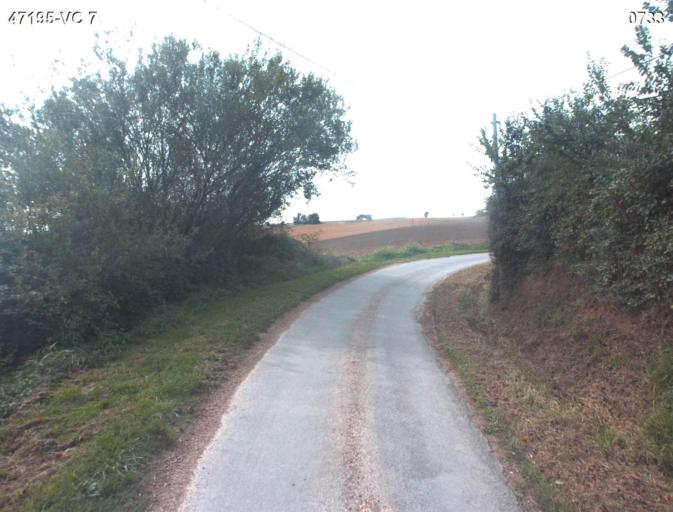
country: FR
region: Aquitaine
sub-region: Departement du Lot-et-Garonne
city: Nerac
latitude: 44.1074
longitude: 0.3468
